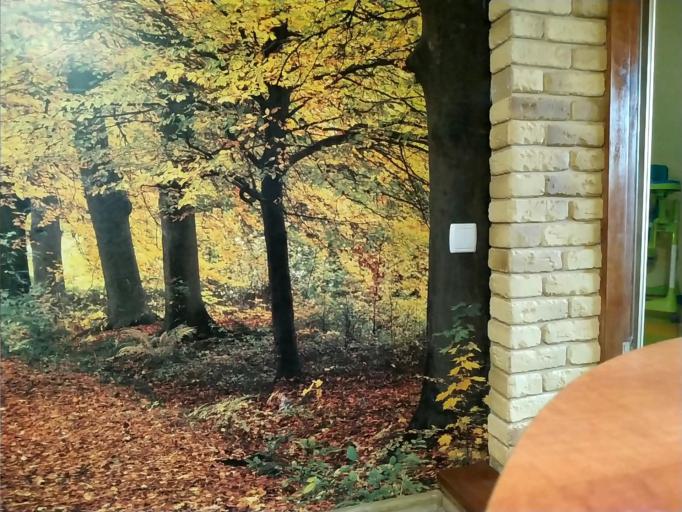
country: RU
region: Leningrad
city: Tolmachevo
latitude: 58.9294
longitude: 29.7224
